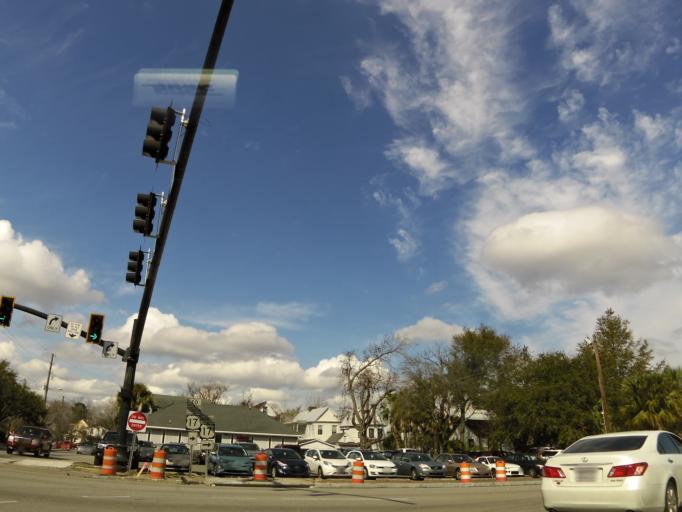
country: US
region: South Carolina
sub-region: Charleston County
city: Charleston
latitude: 32.7867
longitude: -79.9523
